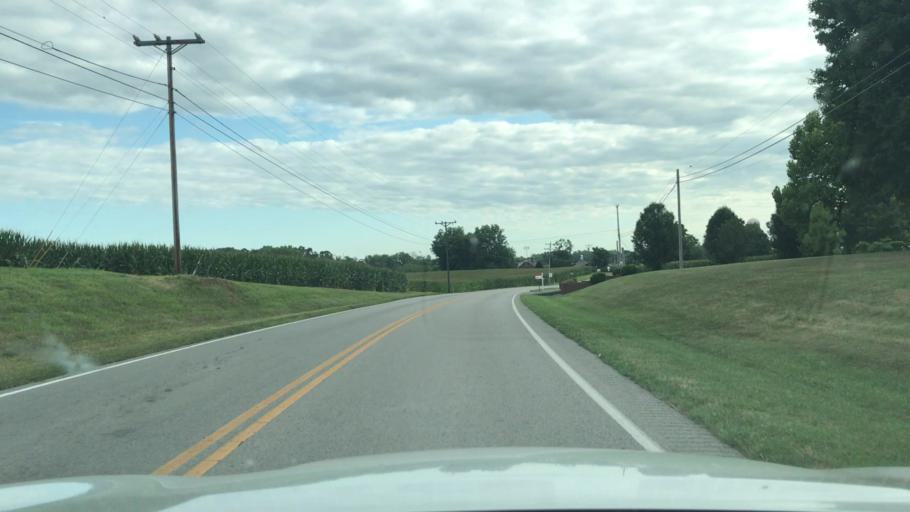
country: US
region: Kentucky
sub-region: Todd County
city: Elkton
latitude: 36.7907
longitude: -87.1640
